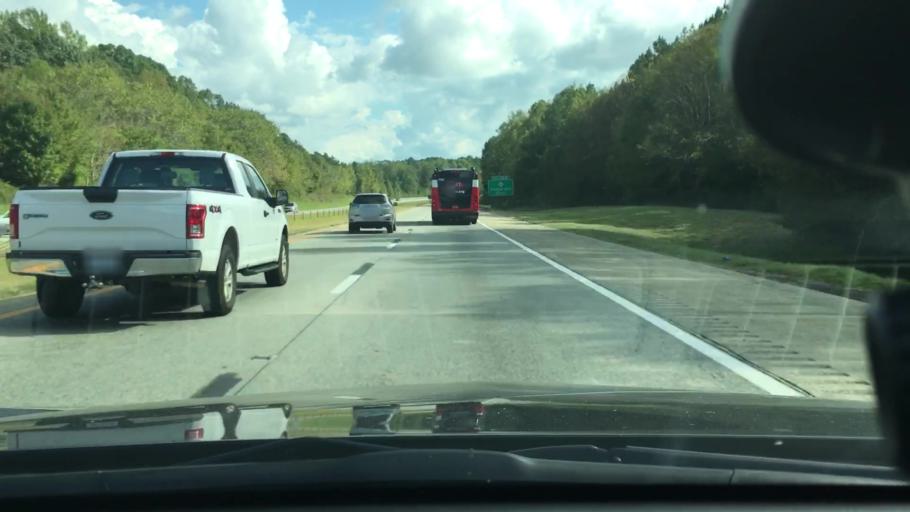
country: US
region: North Carolina
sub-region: Orange County
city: Hillsborough
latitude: 35.9998
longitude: -79.0782
